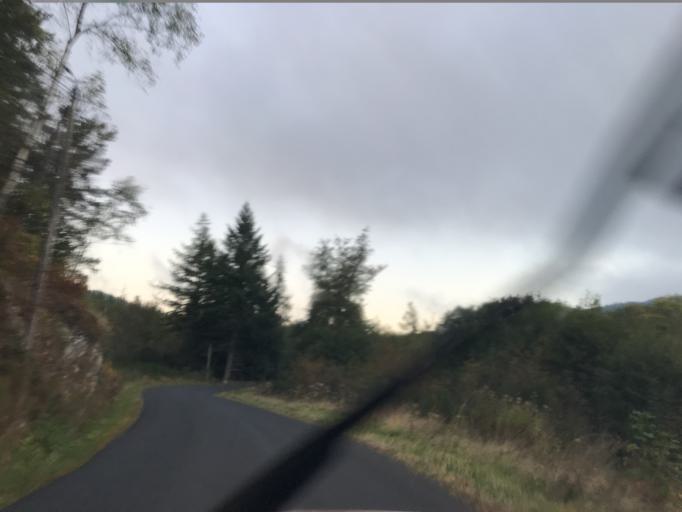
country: FR
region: Auvergne
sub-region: Departement du Puy-de-Dome
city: Celles-sur-Durolle
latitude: 45.7881
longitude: 3.6733
